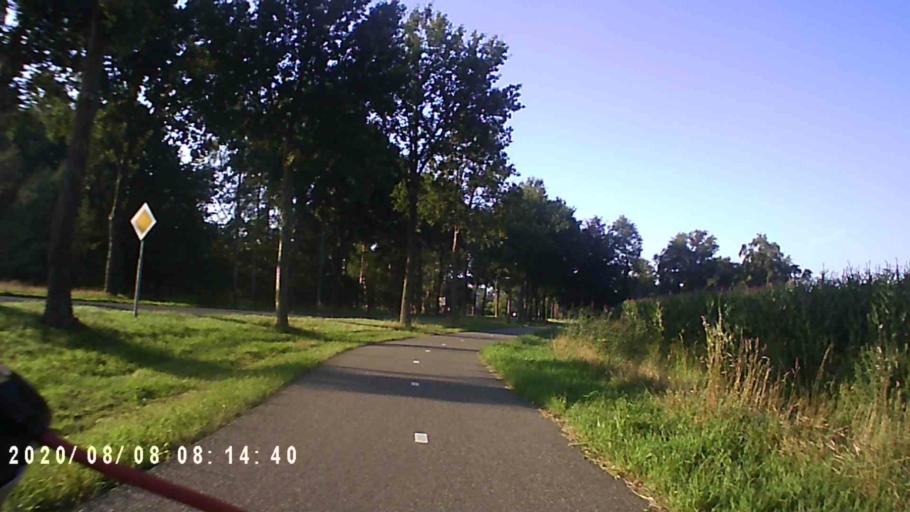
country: NL
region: Groningen
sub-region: Gemeente Leek
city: Leek
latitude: 53.0959
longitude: 6.3413
